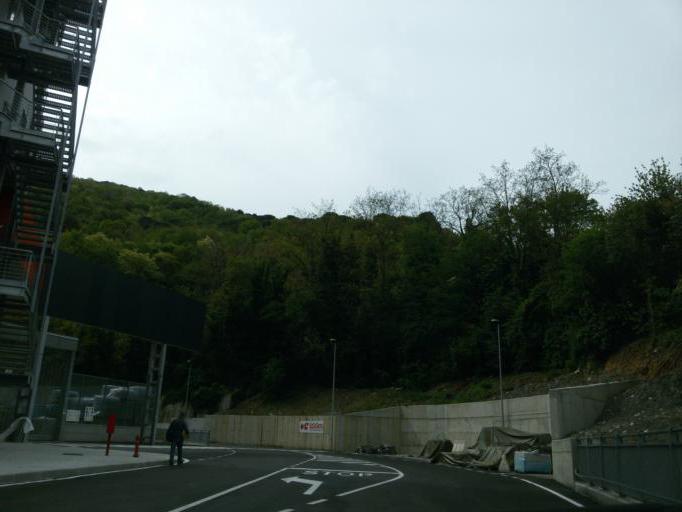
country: IT
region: Liguria
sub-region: Provincia di Genova
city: Piccarello
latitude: 44.4348
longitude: 8.9661
